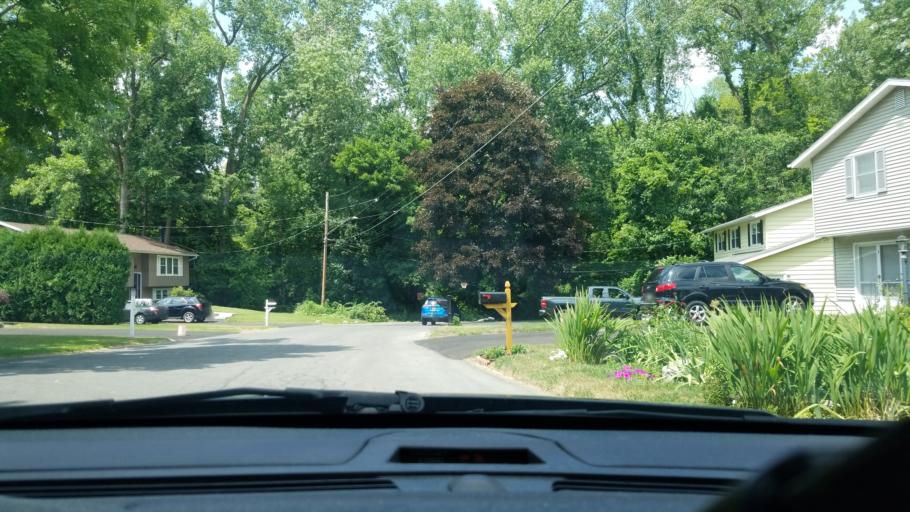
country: US
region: New York
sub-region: Onondaga County
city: Liverpool
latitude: 43.1458
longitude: -76.2262
